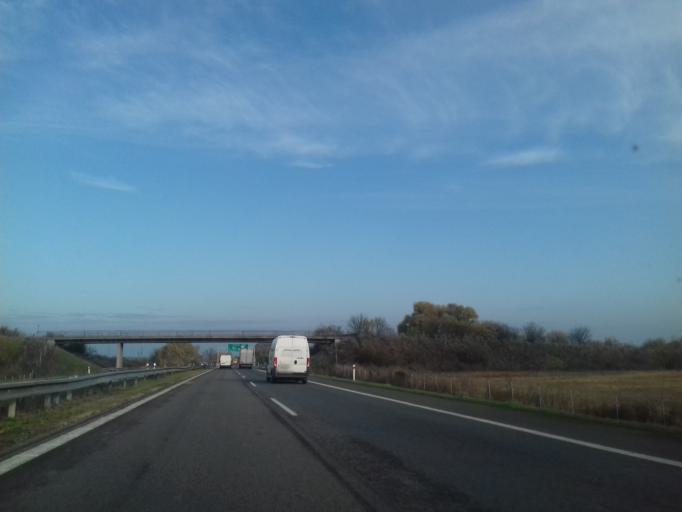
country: SK
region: Bratislavsky
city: Stupava
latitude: 48.2345
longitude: 17.0194
